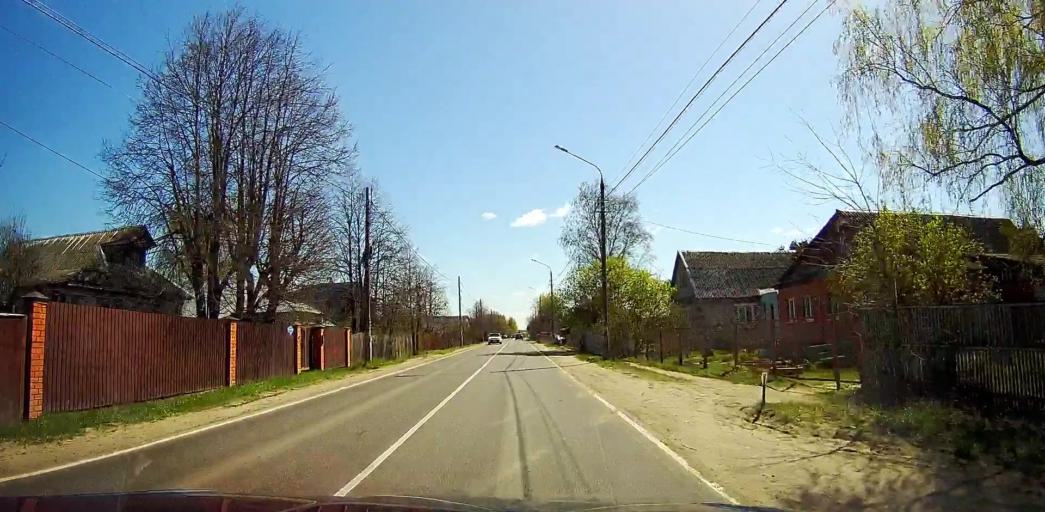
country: RU
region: Moskovskaya
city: Rechitsy
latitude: 55.5379
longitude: 38.4245
